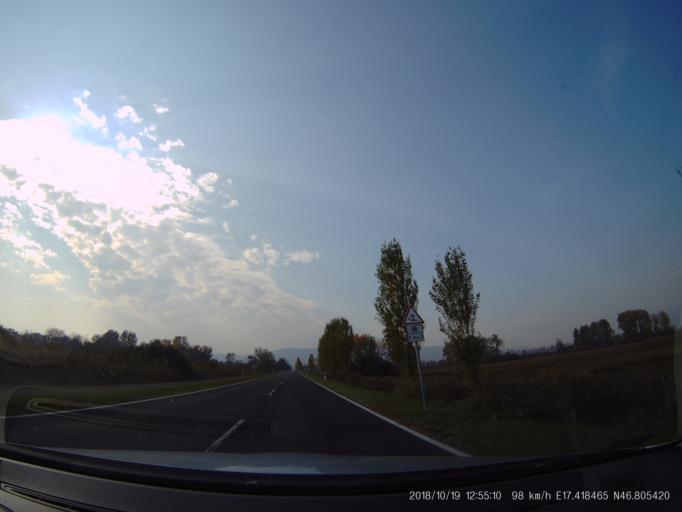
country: HU
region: Veszprem
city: Tapolca
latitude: 46.8054
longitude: 17.4184
